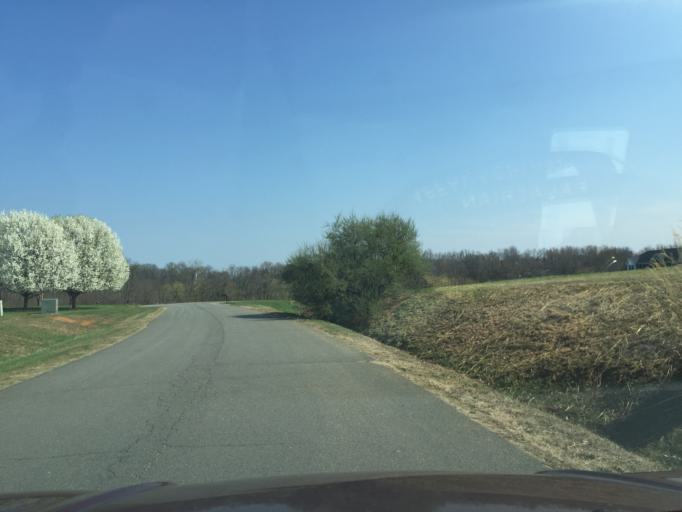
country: US
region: Maryland
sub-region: Frederick County
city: Brunswick
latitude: 39.2948
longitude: -77.5925
